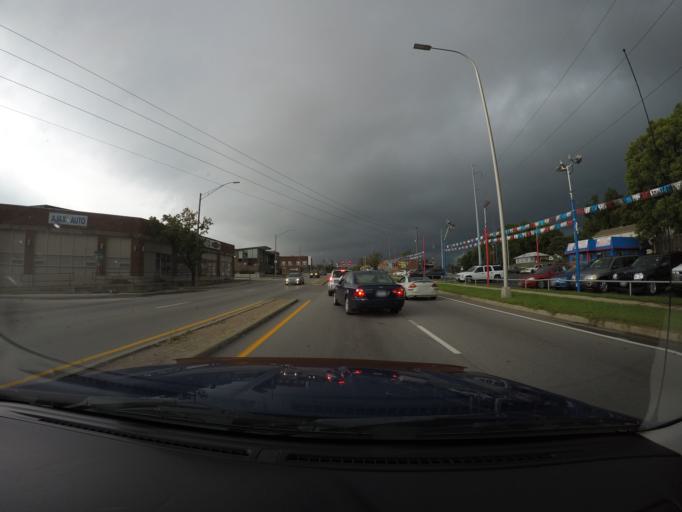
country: US
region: Missouri
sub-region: Jackson County
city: Sugar Creek
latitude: 39.1028
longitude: -94.4547
